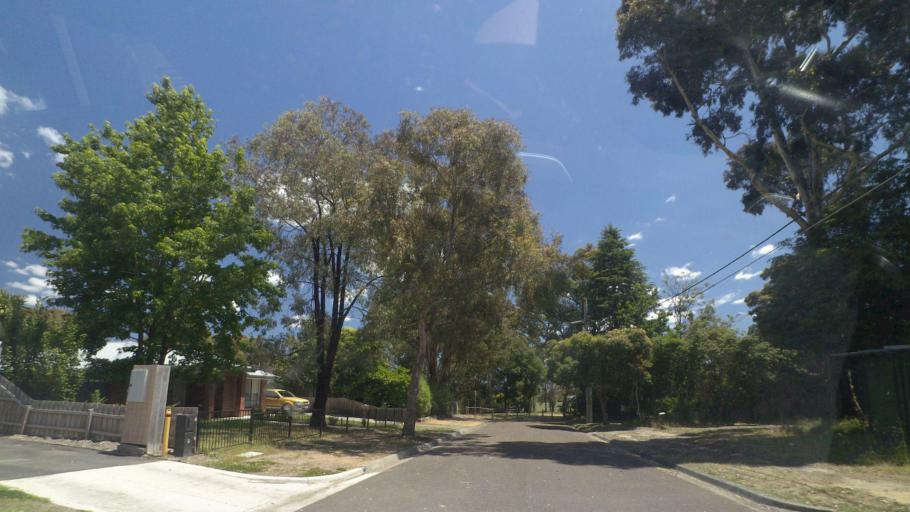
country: AU
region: Victoria
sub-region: Maroondah
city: Kilsyth South
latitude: -37.8129
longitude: 145.3227
